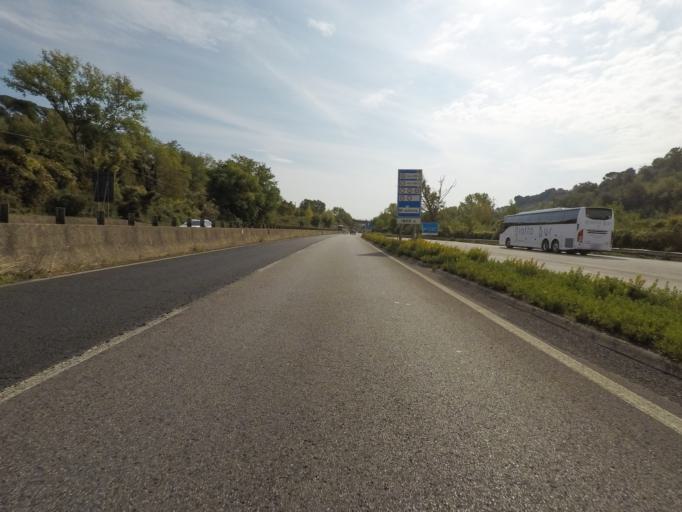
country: IT
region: Tuscany
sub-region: Provincia di Siena
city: Siena
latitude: 43.3130
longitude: 11.3095
